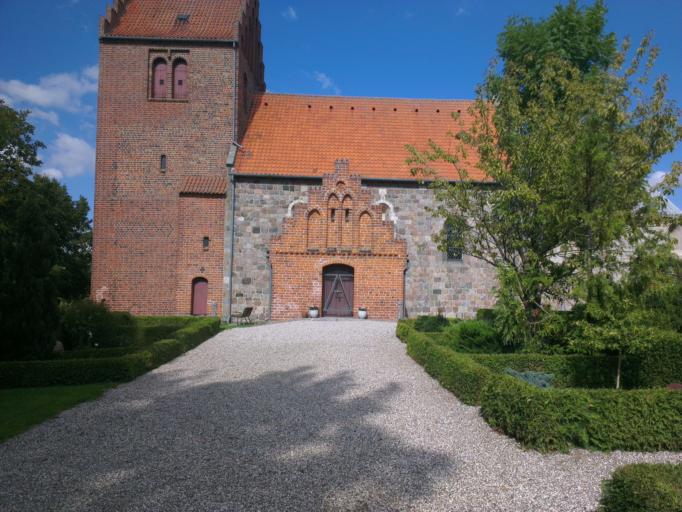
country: DK
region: Capital Region
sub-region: Frederikssund Kommune
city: Skibby
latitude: 55.7433
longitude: 12.0059
